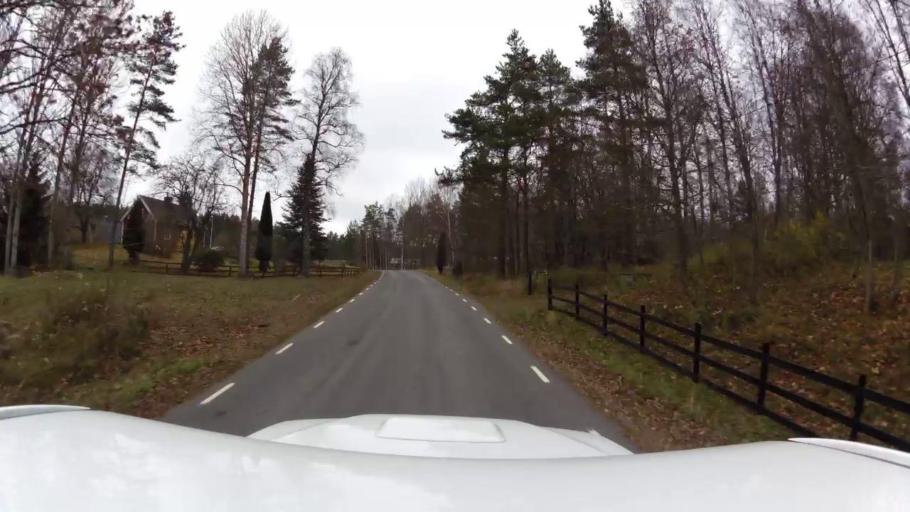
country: SE
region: OEstergoetland
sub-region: Kinda Kommun
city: Kisa
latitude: 58.1317
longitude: 15.4536
